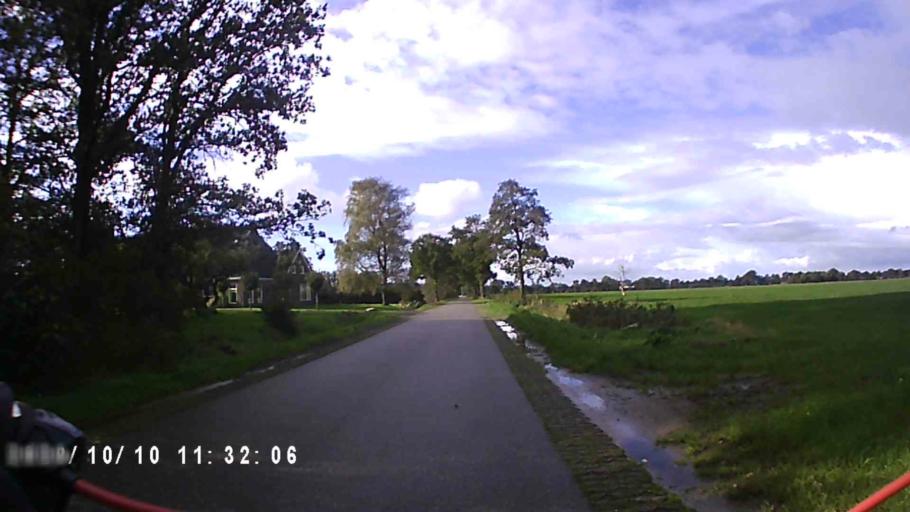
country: NL
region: Friesland
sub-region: Gemeente Smallingerland
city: Drachten
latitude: 53.0830
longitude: 6.1355
